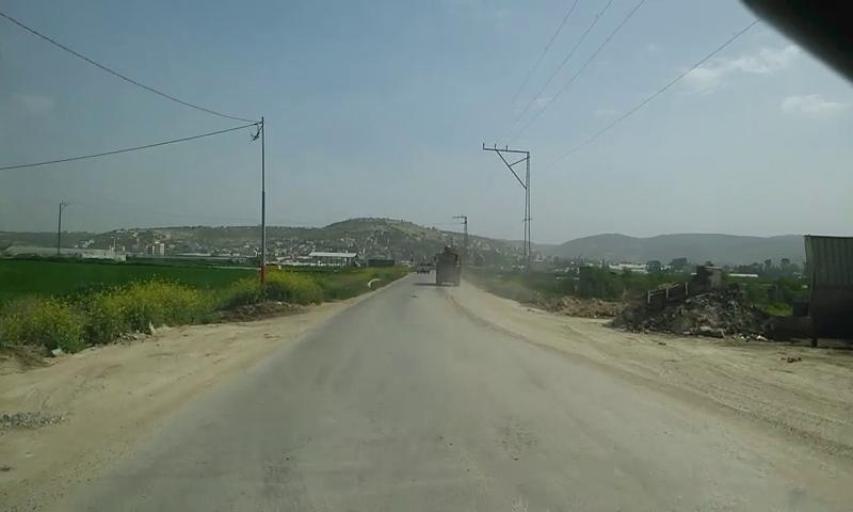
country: PS
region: West Bank
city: Ash Shuhada'
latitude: 32.4369
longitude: 35.2652
